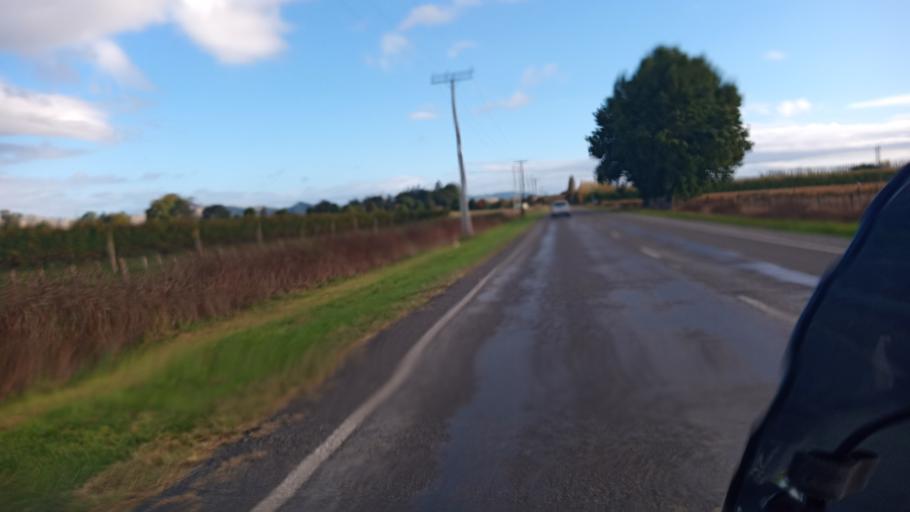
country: NZ
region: Gisborne
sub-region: Gisborne District
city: Gisborne
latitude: -38.6447
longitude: 177.9169
